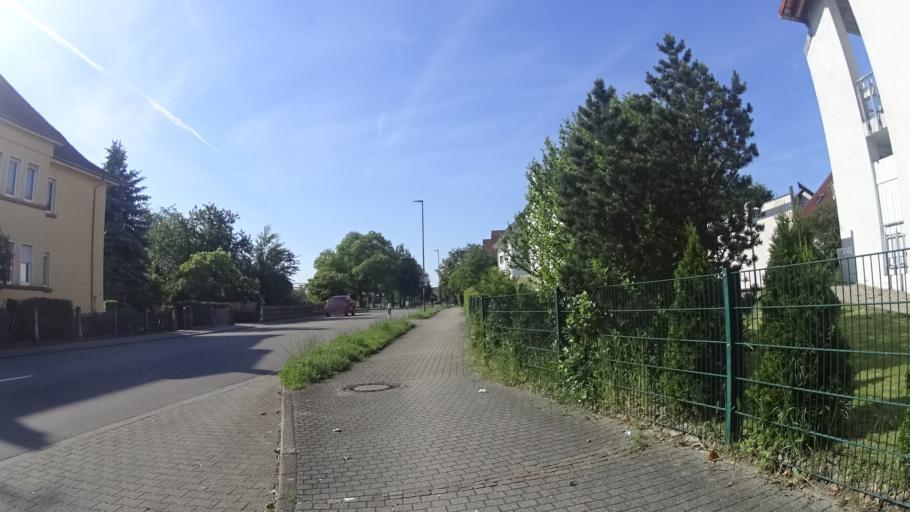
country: DE
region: Baden-Wuerttemberg
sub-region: Freiburg Region
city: Kehl
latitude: 48.5545
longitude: 7.8359
